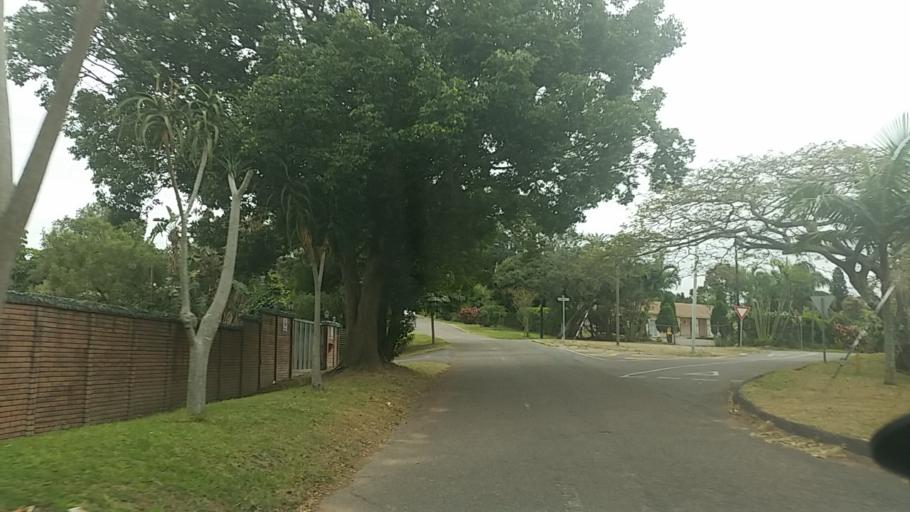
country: ZA
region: KwaZulu-Natal
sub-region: eThekwini Metropolitan Municipality
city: Berea
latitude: -29.8445
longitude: 30.9350
